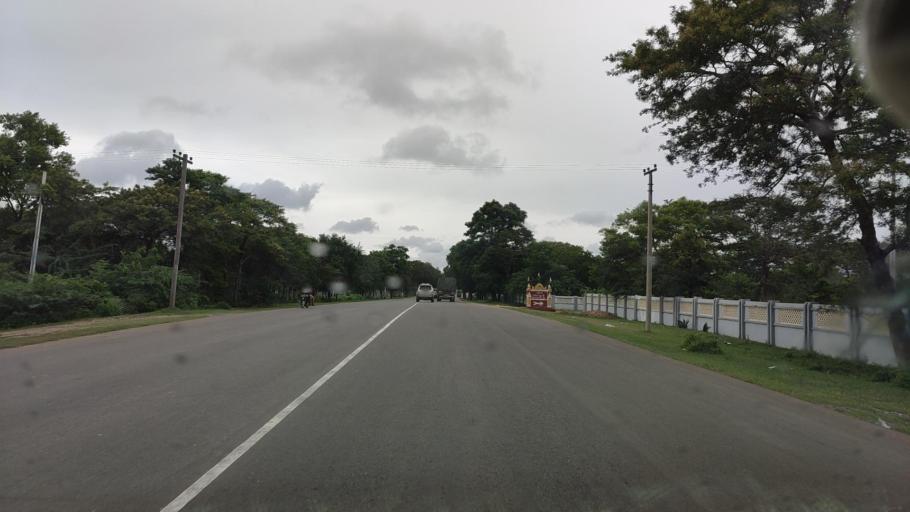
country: MM
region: Mandalay
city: Meiktila
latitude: 20.8382
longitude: 95.8948
